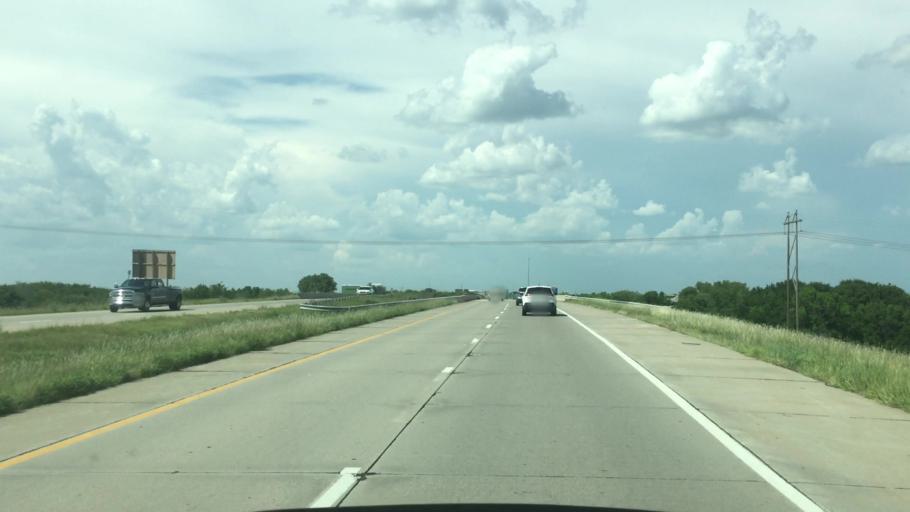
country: US
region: Kansas
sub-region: Butler County
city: Andover
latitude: 37.7145
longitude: -97.1995
